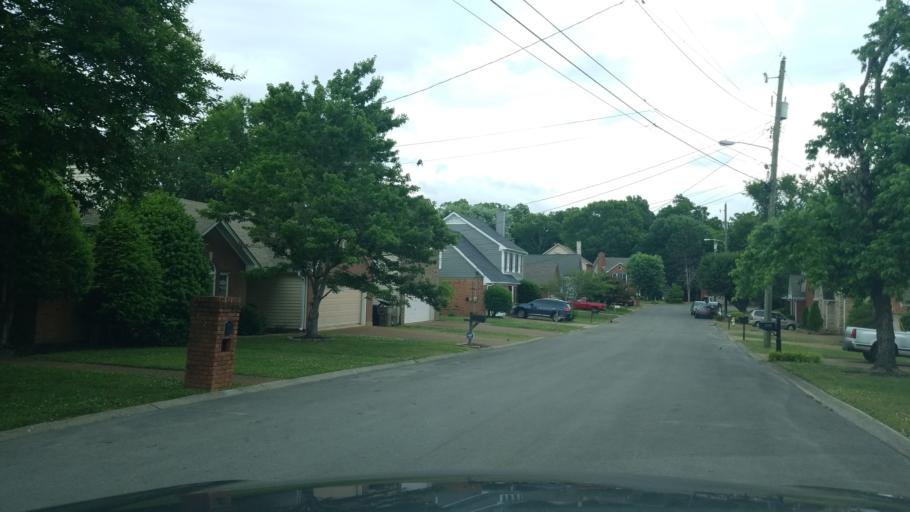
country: US
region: Tennessee
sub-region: Rutherford County
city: La Vergne
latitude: 36.0816
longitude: -86.5871
